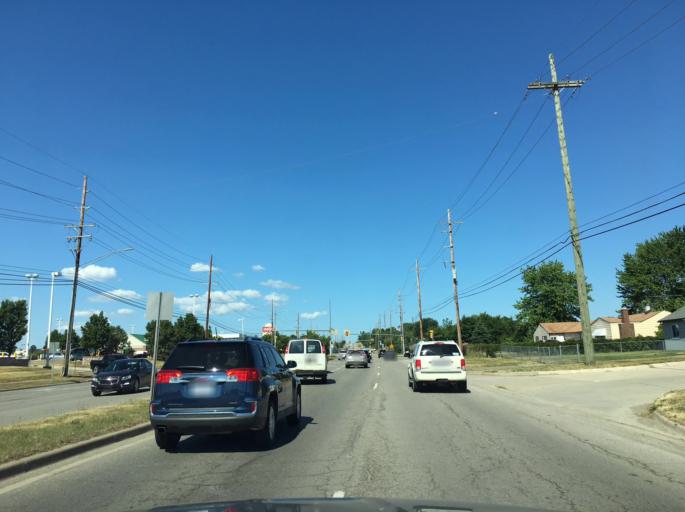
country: US
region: Michigan
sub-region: Oakland County
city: Auburn Hills
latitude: 42.7077
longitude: -83.2860
